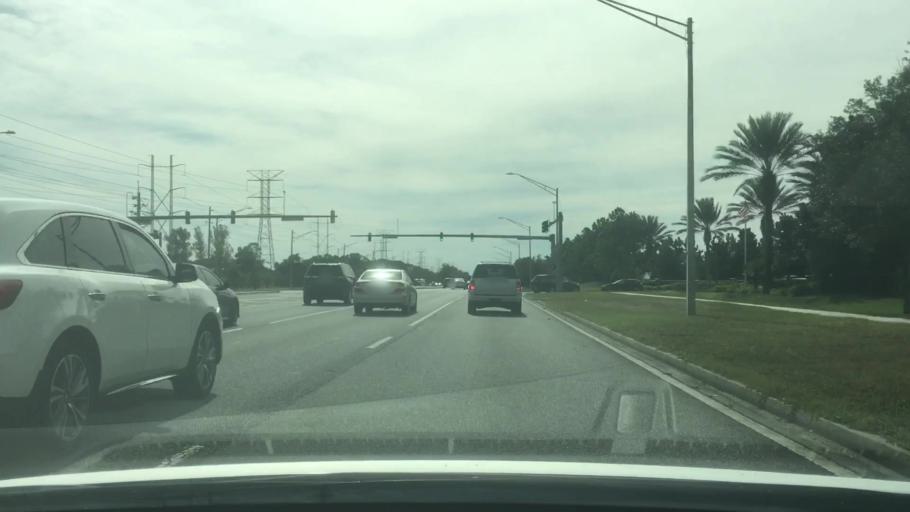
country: US
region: Florida
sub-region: Duval County
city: Neptune Beach
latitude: 30.3127
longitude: -81.4894
